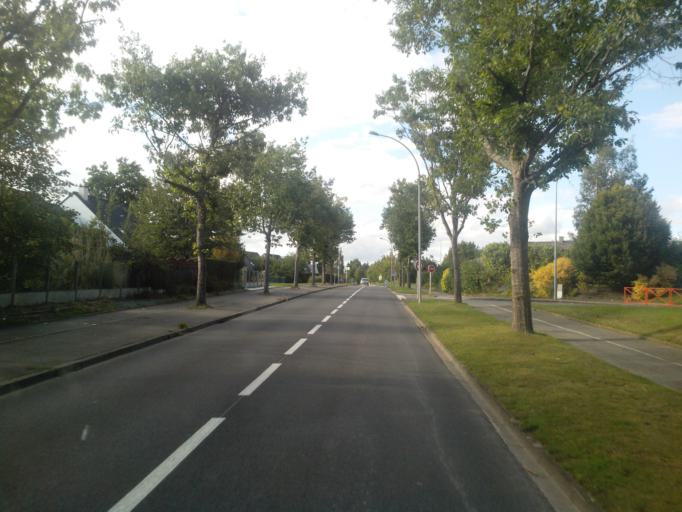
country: FR
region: Brittany
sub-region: Departement d'Ille-et-Vilaine
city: Montfort-sur-Meu
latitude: 48.1403
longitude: -1.9634
